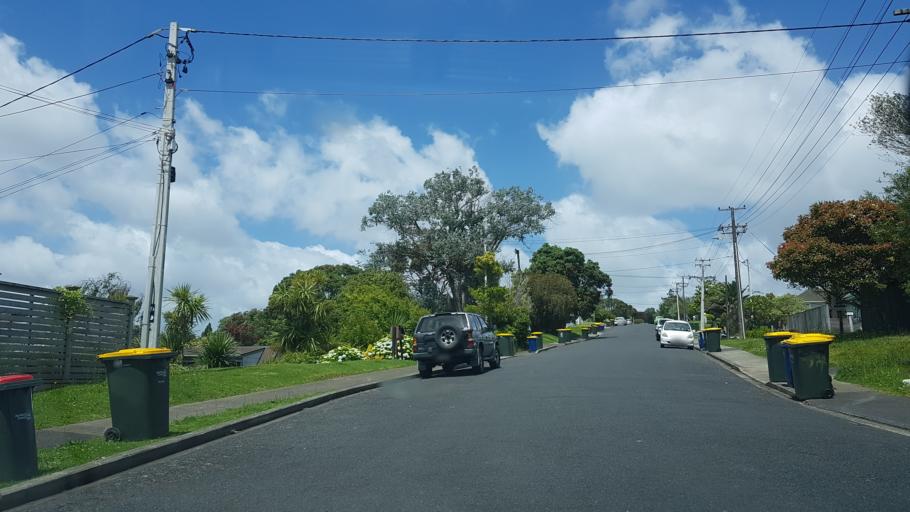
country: NZ
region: Auckland
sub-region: Auckland
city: North Shore
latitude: -36.8040
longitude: 174.7125
